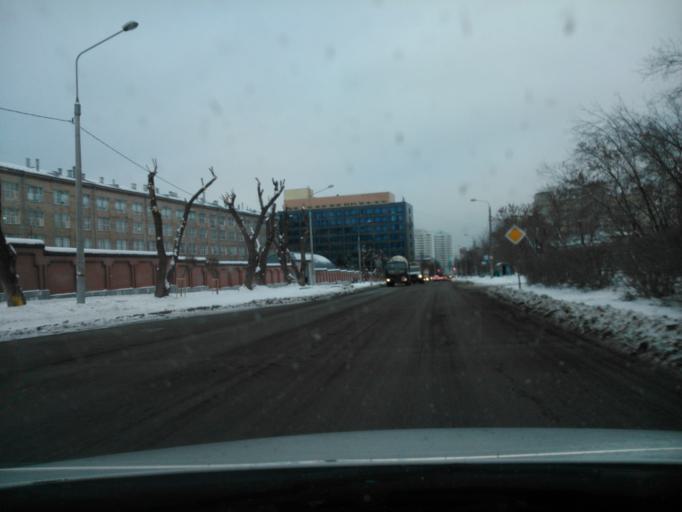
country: RU
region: Perm
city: Perm
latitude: 57.9892
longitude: 56.2012
